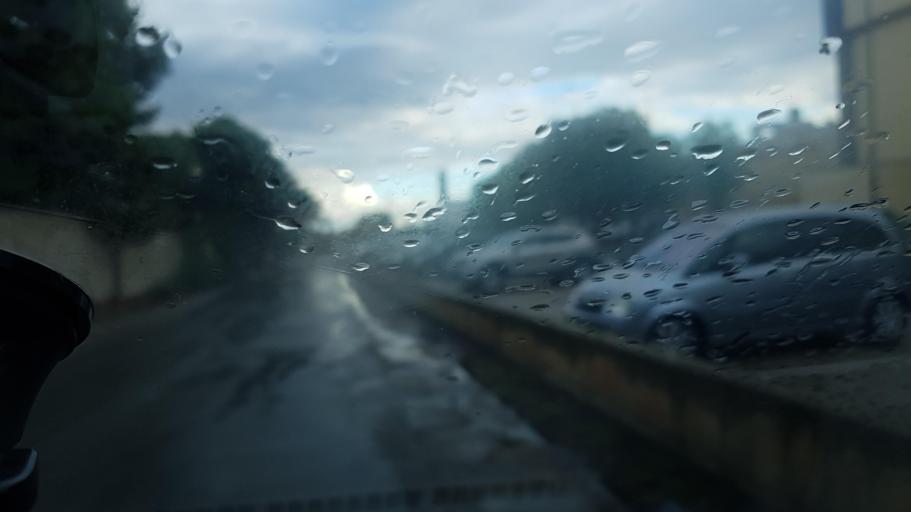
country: IT
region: Apulia
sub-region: Provincia di Lecce
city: Giorgilorio
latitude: 40.3770
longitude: 18.1476
